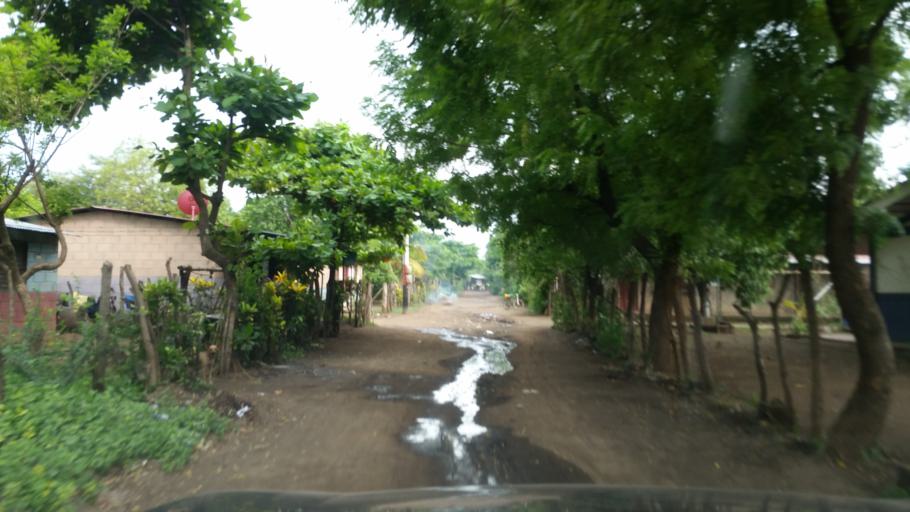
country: NI
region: Chinandega
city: Puerto Morazan
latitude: 12.7660
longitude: -87.1263
